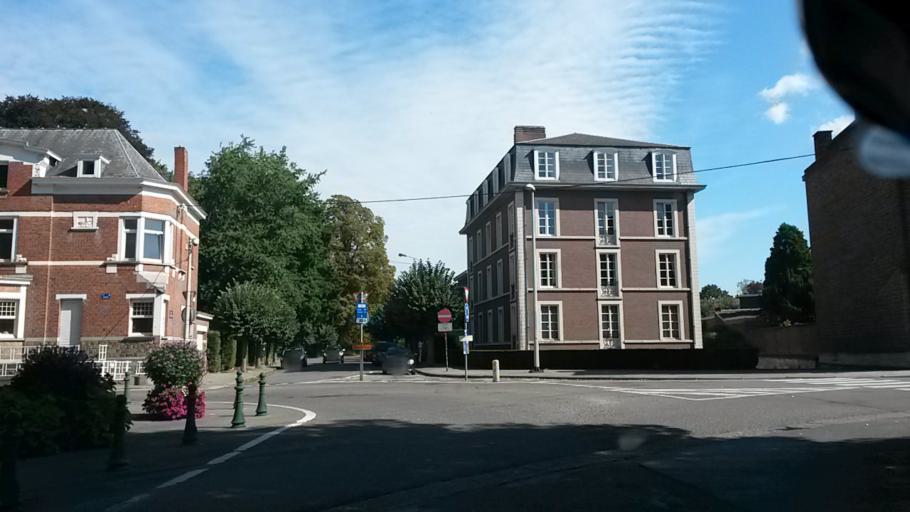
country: BE
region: Wallonia
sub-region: Province de Liege
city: Huy
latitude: 50.5249
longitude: 5.2434
